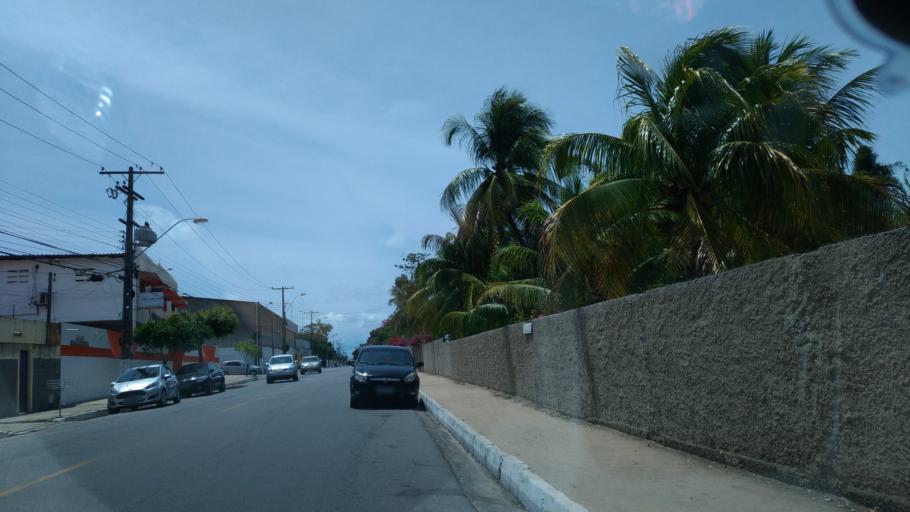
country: BR
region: Alagoas
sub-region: Maceio
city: Maceio
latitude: -9.6114
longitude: -35.7212
